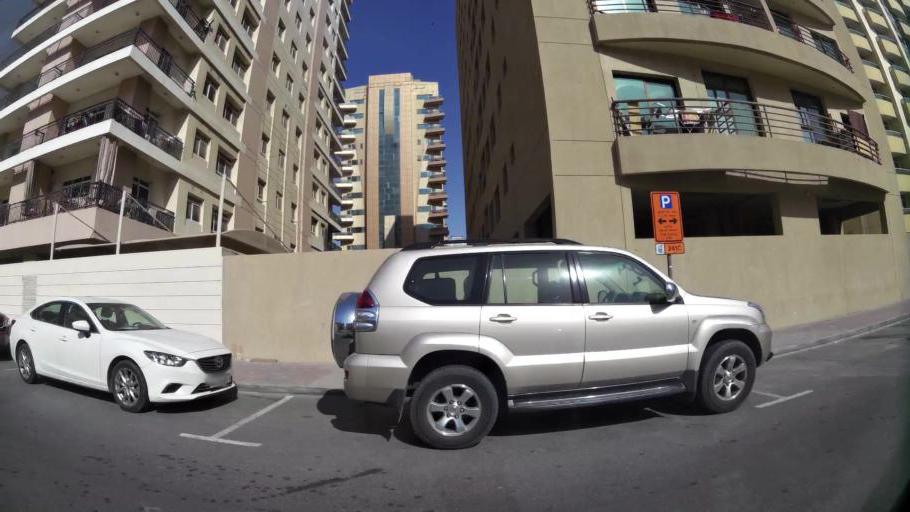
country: AE
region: Ash Shariqah
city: Sharjah
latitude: 25.2940
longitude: 55.3810
